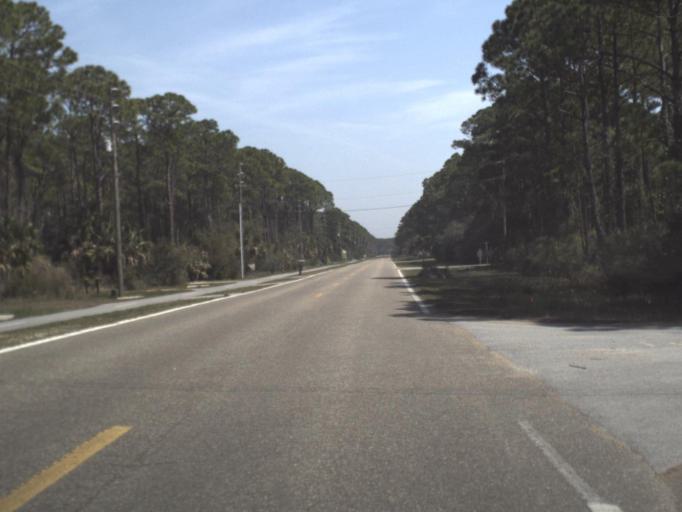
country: US
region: Florida
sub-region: Gulf County
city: Port Saint Joe
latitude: 29.6838
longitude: -85.3249
